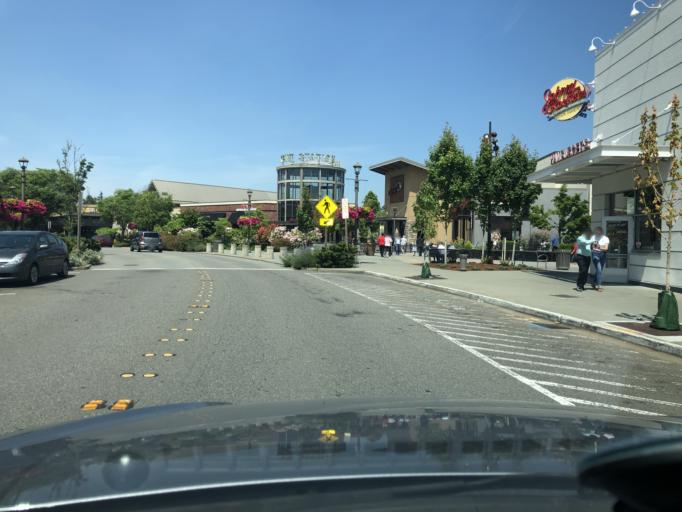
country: US
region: Washington
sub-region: King County
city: Kent
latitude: 47.3844
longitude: -122.2348
